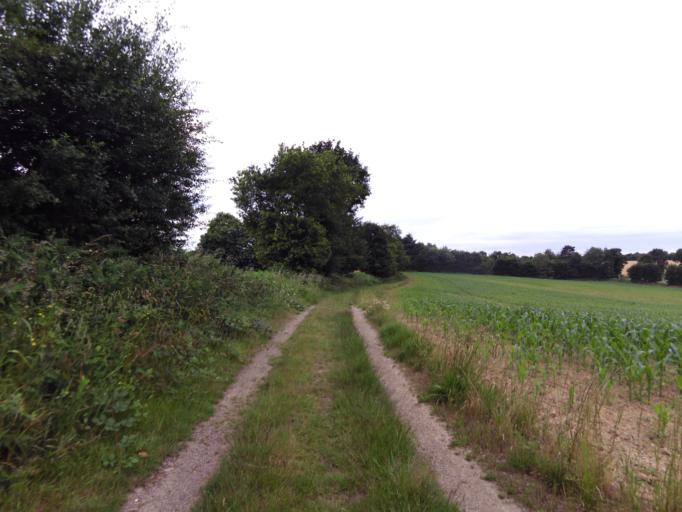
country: FR
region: Brittany
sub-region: Departement d'Ille-et-Vilaine
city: Chanteloup
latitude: 47.9306
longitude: -1.5970
